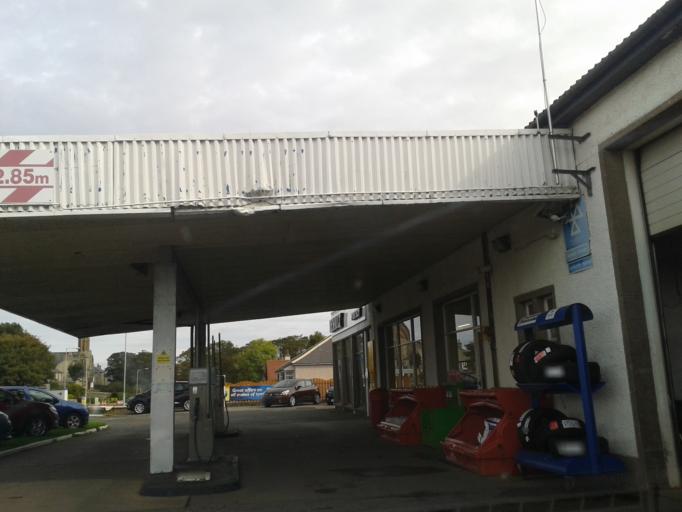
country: GB
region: Scotland
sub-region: Aberdeenshire
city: Portsoy
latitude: 57.6794
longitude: -2.6970
